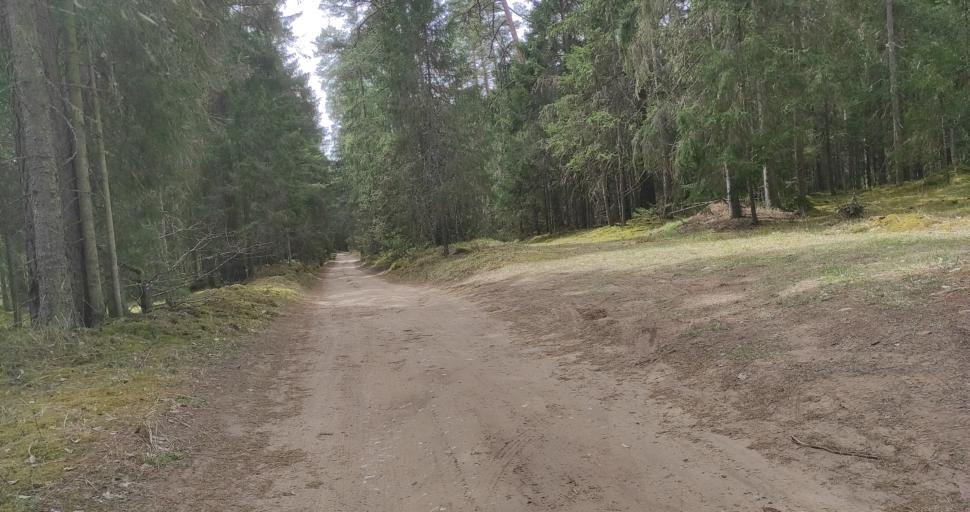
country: LV
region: Talsu Rajons
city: Stende
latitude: 57.0861
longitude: 22.3915
